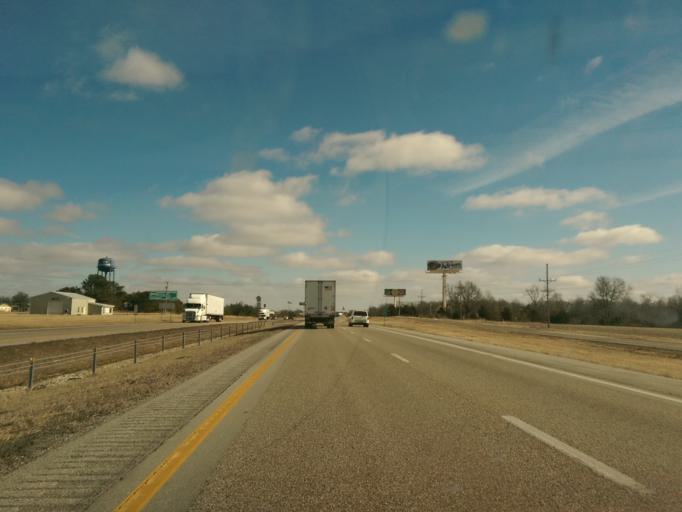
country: US
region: Missouri
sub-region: Montgomery County
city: Montgomery City
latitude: 38.9025
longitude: -91.4742
